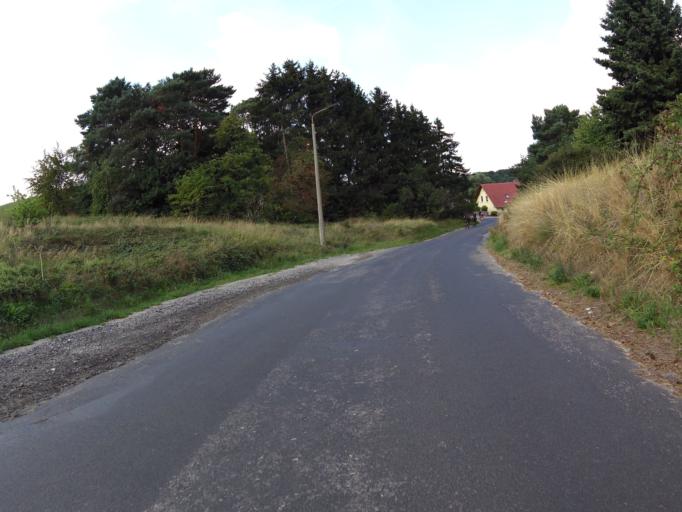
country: DE
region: Mecklenburg-Vorpommern
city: Seebad Bansin
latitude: 53.9596
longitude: 14.1204
